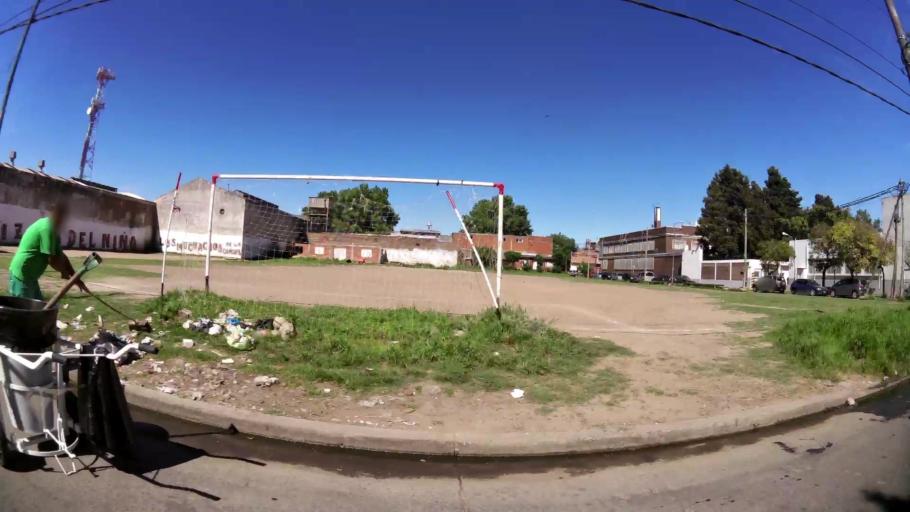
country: AR
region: Buenos Aires
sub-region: Partido de General San Martin
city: General San Martin
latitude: -34.5547
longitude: -58.5245
